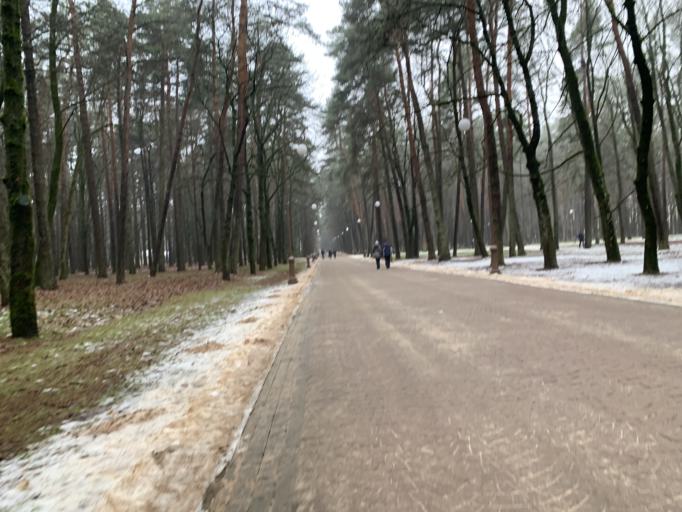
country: BY
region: Minsk
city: Minsk
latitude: 53.9219
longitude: 27.6158
